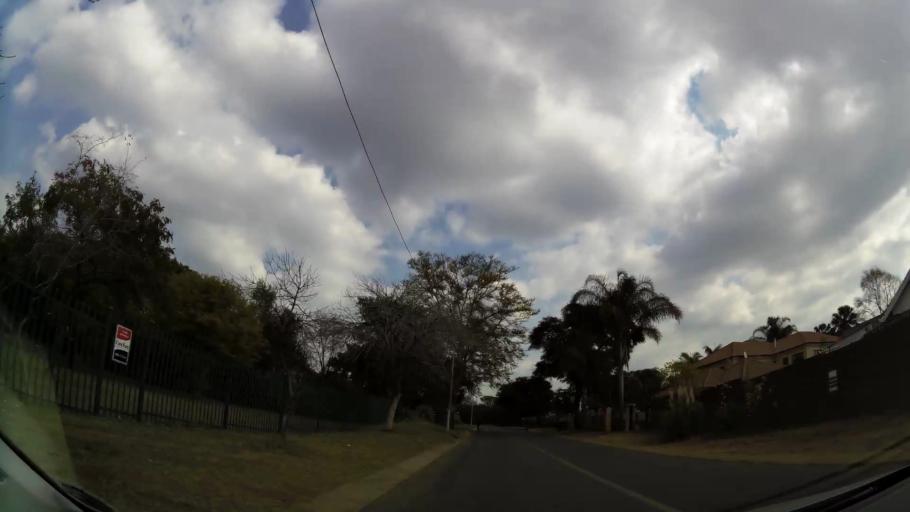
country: ZA
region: Gauteng
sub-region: City of Tshwane Metropolitan Municipality
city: Pretoria
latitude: -25.7615
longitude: 28.3187
